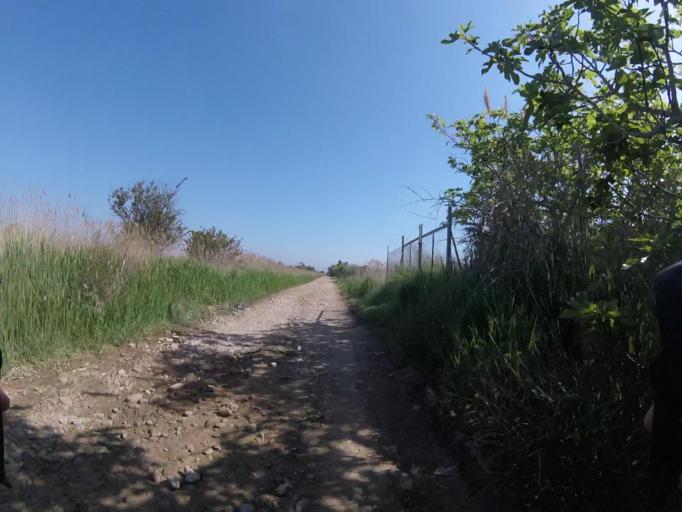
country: ES
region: Valencia
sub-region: Provincia de Castello
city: Orpesa/Oropesa del Mar
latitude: 40.1506
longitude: 0.1670
